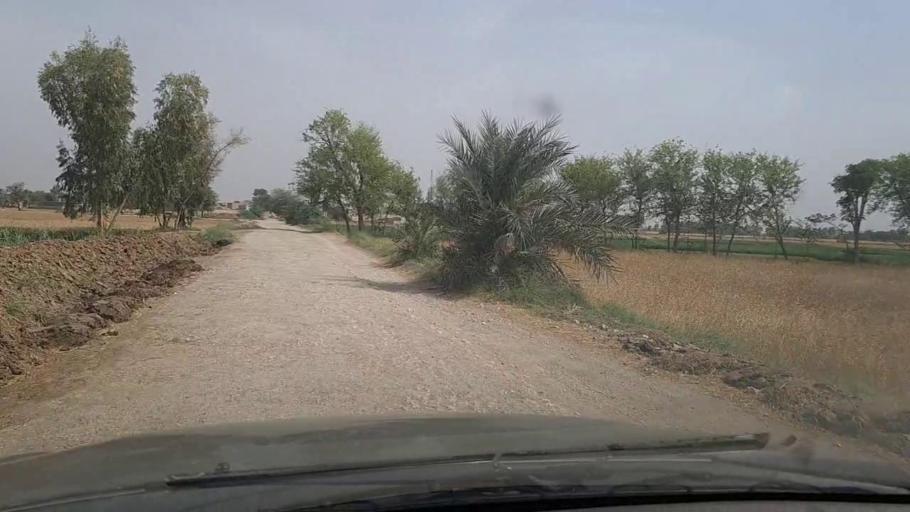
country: PK
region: Sindh
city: Chak
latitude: 27.8335
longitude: 68.7716
